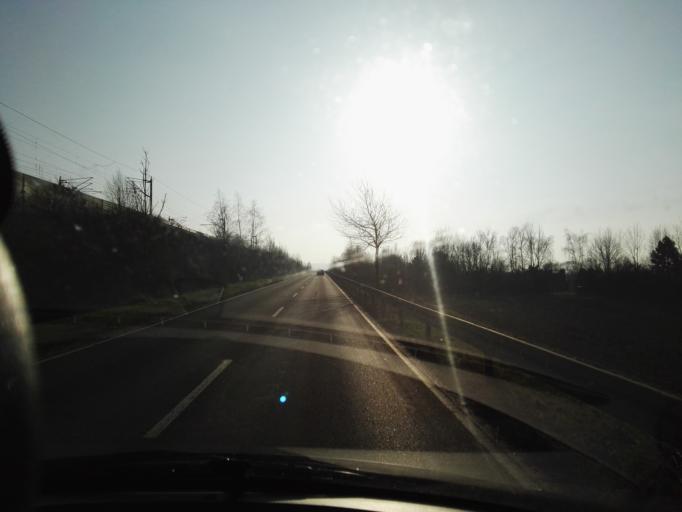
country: DE
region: Lower Saxony
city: Sarstedt
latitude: 52.2037
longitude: 9.8237
